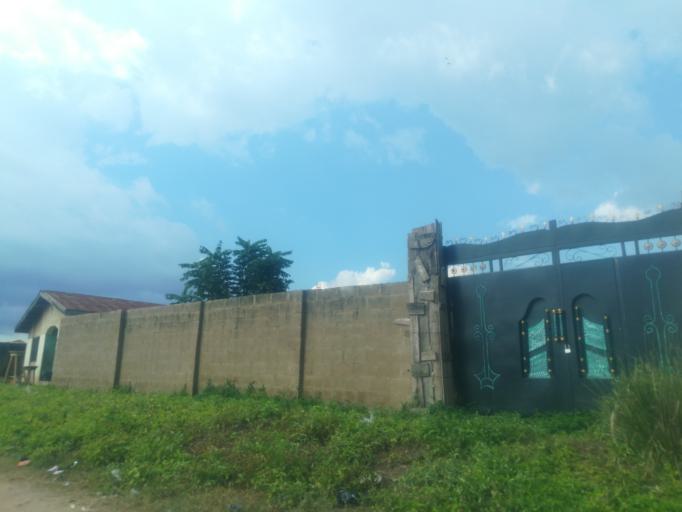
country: NG
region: Oyo
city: Ibadan
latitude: 7.4194
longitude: 3.8421
